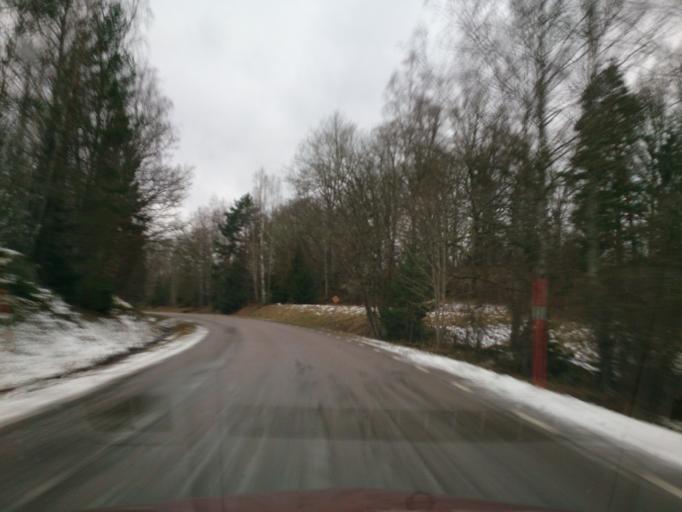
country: SE
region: OEstergoetland
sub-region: Atvidabergs Kommun
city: Atvidaberg
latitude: 58.2638
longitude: 16.0285
